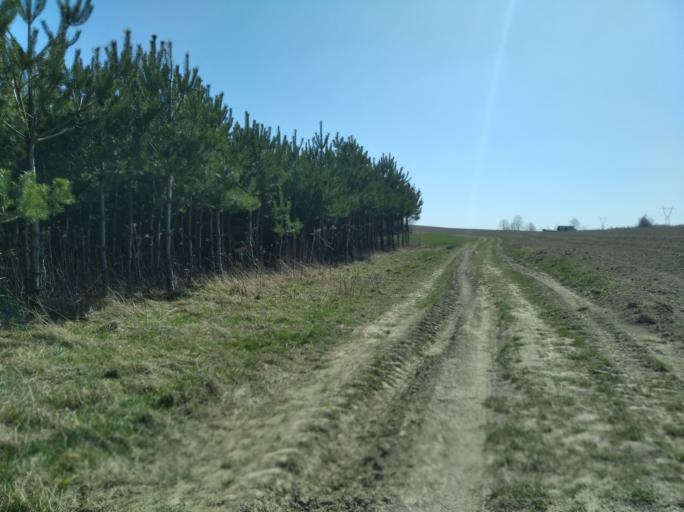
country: PL
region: Subcarpathian Voivodeship
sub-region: Powiat strzyzowski
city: Polomia
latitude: 49.8806
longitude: 21.8568
